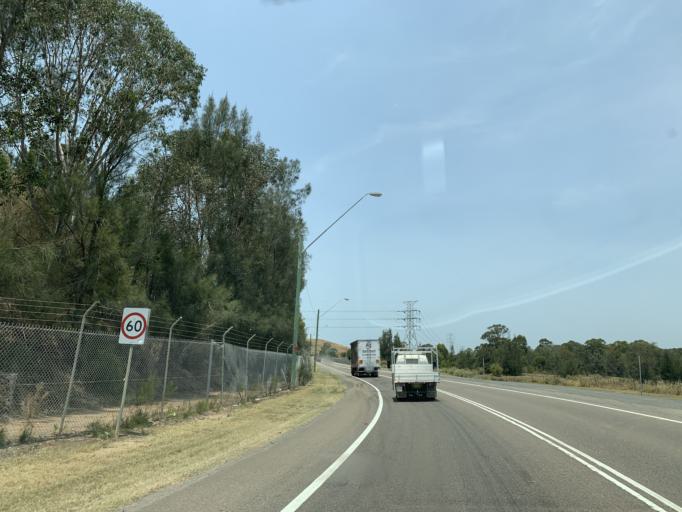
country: AU
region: New South Wales
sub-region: Blacktown
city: Doonside
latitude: -33.8028
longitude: 150.8646
